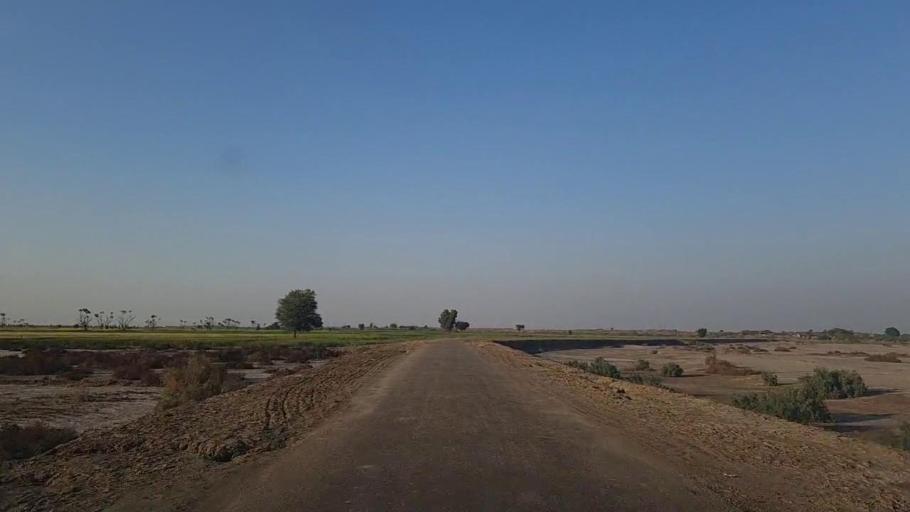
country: PK
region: Sindh
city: Jam Sahib
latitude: 26.3360
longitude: 68.6676
